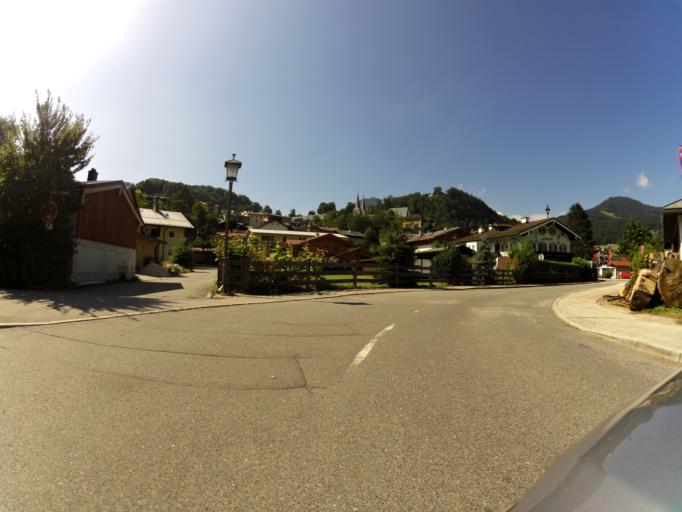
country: DE
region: Bavaria
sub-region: Upper Bavaria
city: Berchtesgaden
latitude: 47.6307
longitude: 13.0061
